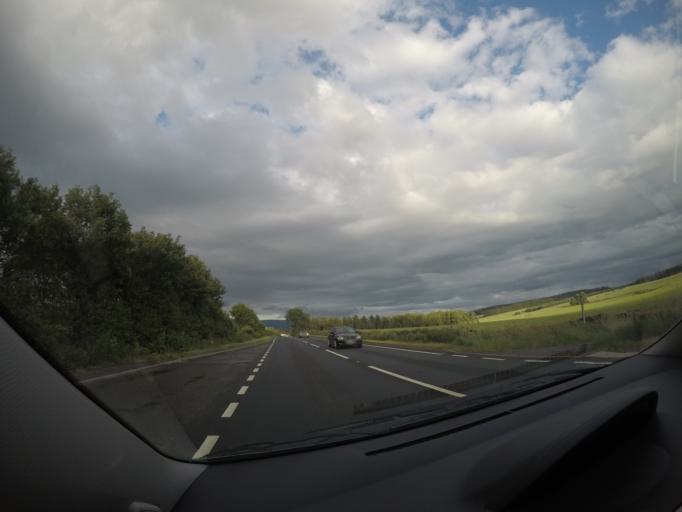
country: GB
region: England
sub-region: Cumbria
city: Penrith
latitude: 54.6525
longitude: -2.6549
